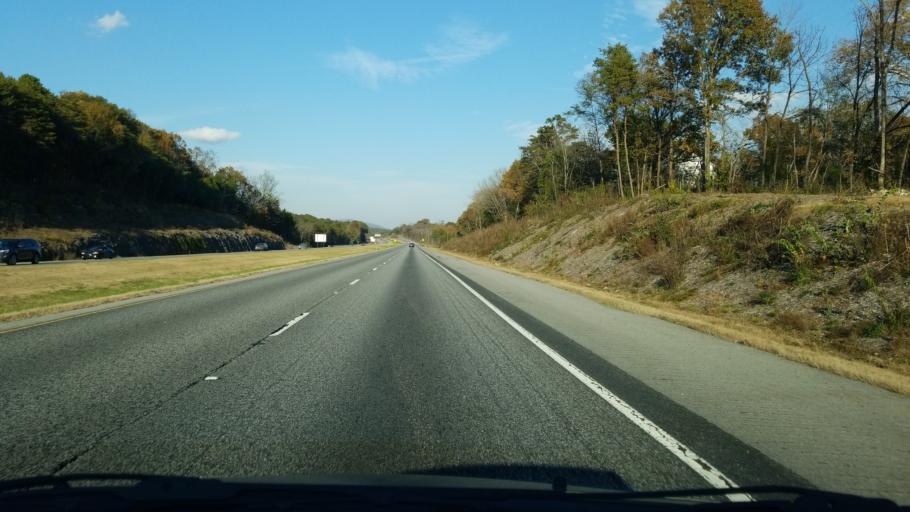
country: US
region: Georgia
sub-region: Dade County
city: Trenton
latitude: 34.8844
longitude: -85.5078
